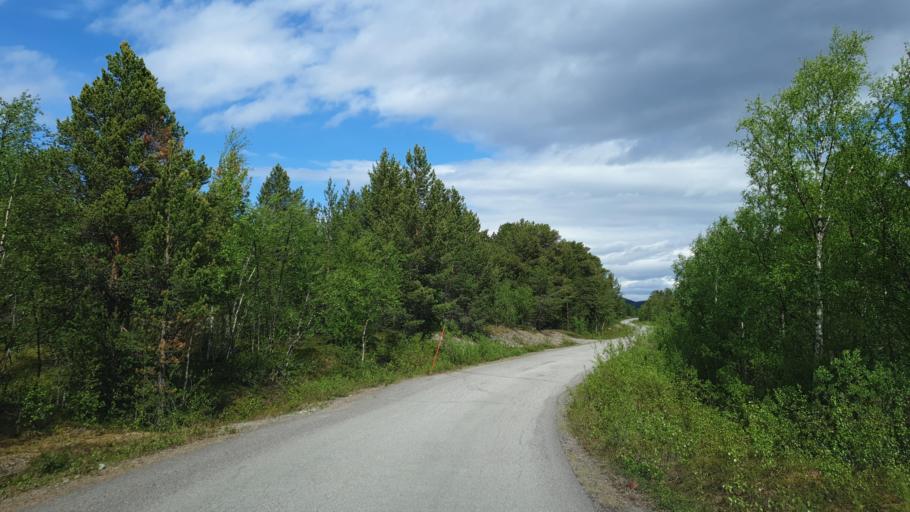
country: SE
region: Norrbotten
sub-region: Kiruna Kommun
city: Kiruna
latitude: 68.2219
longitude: 19.7135
